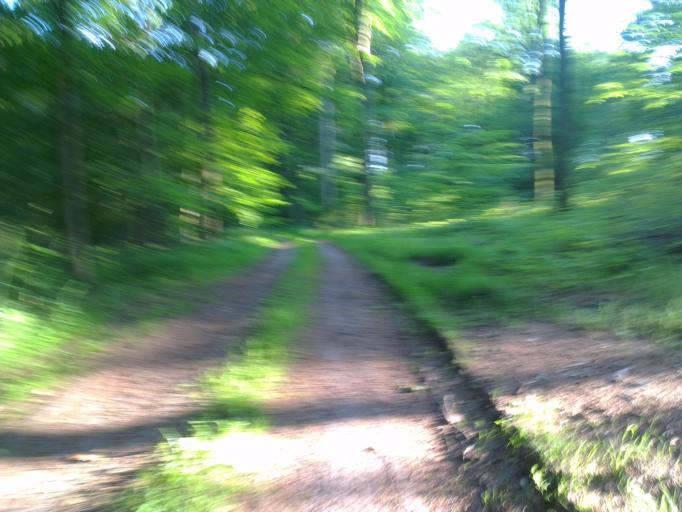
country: DK
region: Capital Region
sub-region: Frederikssund Kommune
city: Jaegerspris
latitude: 55.8967
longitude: 12.0018
